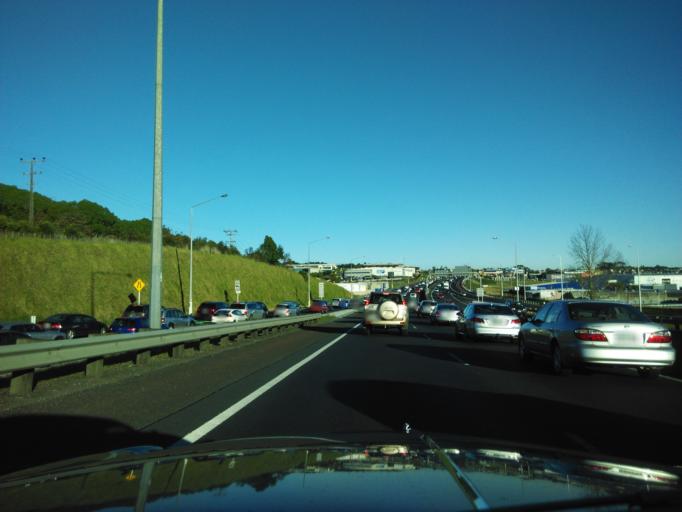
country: NZ
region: Auckland
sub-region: Auckland
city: Rothesay Bay
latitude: -36.7362
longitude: 174.7183
